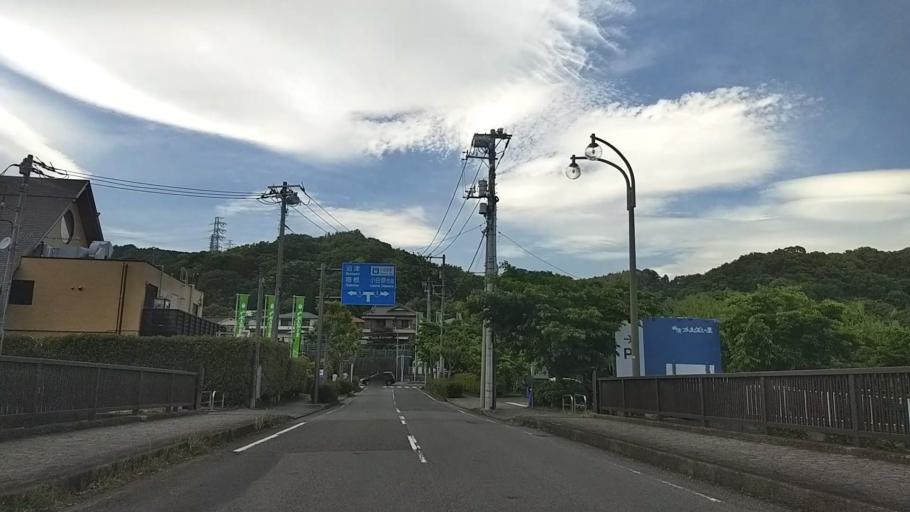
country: JP
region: Kanagawa
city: Odawara
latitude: 35.2456
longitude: 139.1317
